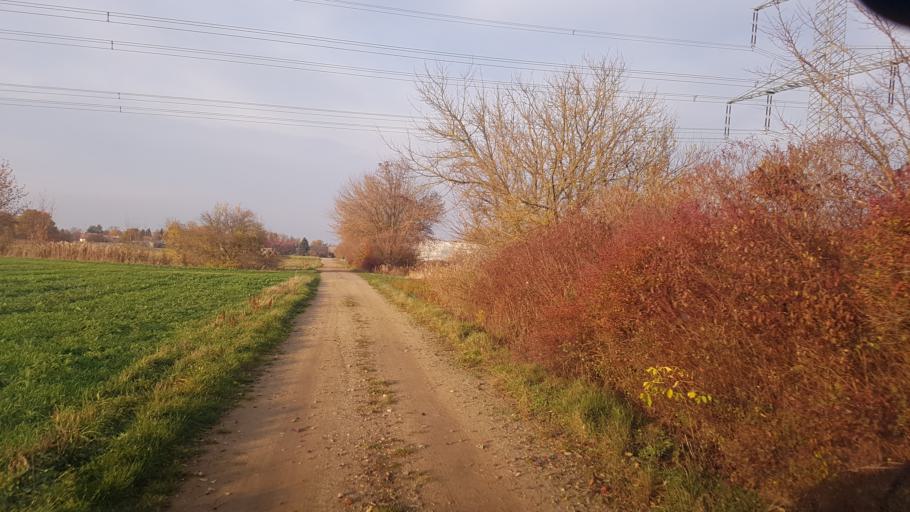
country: DE
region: Brandenburg
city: Schonewalde
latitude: 51.6528
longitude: 13.5988
